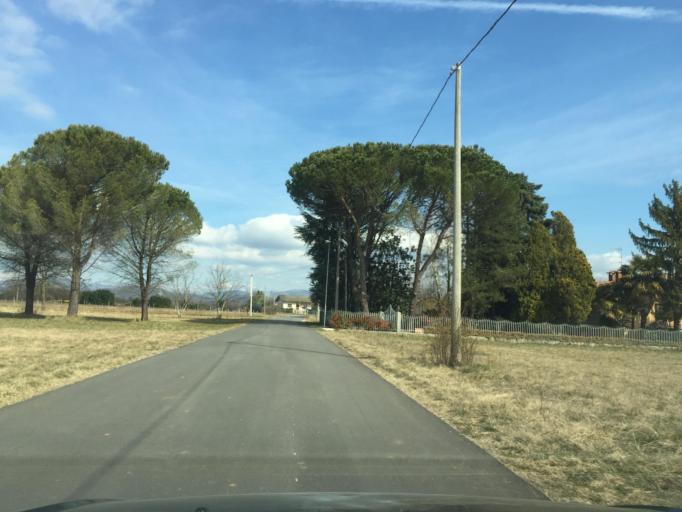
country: IT
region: Friuli Venezia Giulia
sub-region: Provincia di Gorizia
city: Savogna d'Isonzo
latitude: 45.8975
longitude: 13.5911
